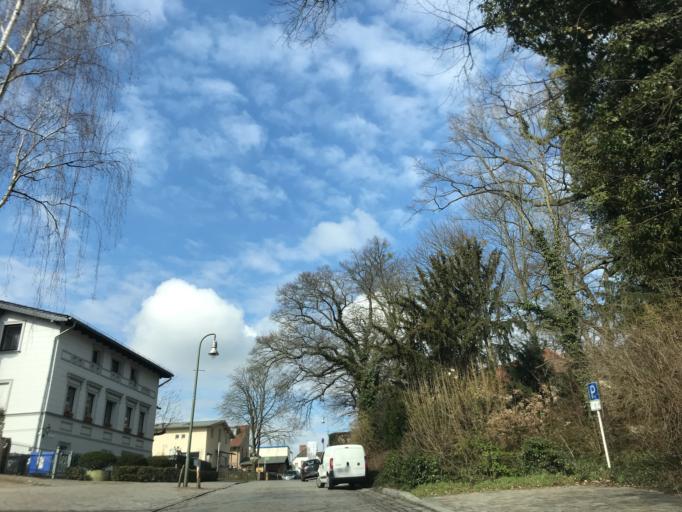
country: DE
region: Berlin
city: Kladow
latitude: 52.4525
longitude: 13.1459
